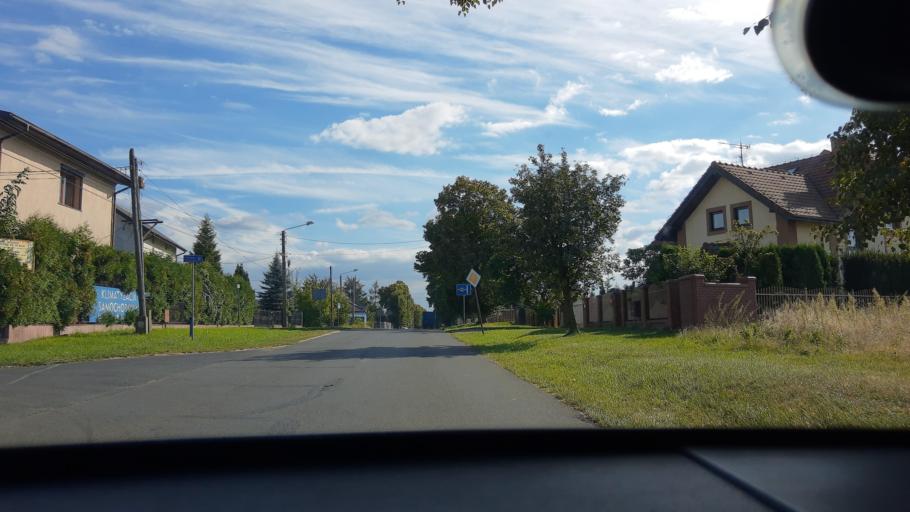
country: PL
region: Lodz Voivodeship
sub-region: Powiat sieradzki
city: Sieradz
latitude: 51.5779
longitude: 18.7369
